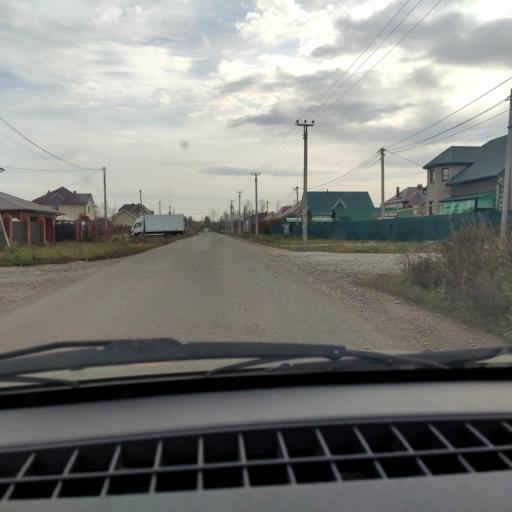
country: RU
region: Bashkortostan
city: Ufa
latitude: 54.6266
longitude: 55.9084
